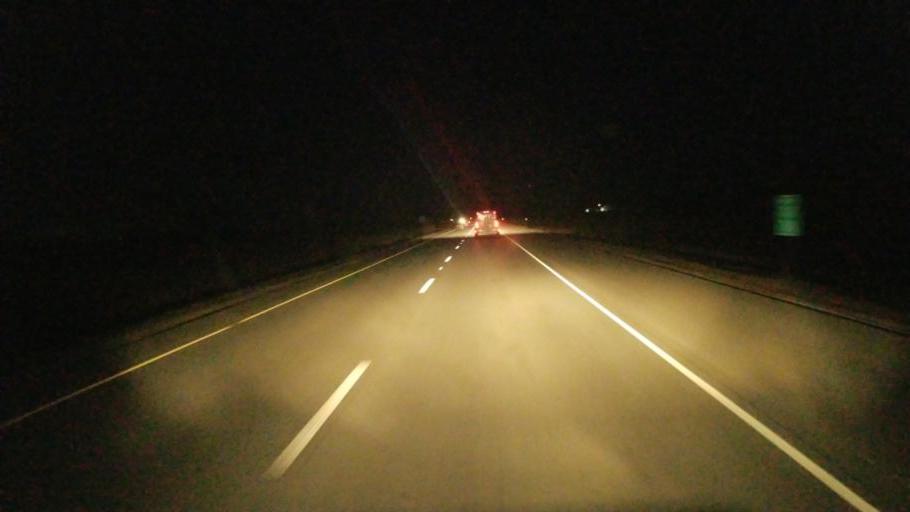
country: US
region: Illinois
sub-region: Henderson County
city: Oquawka
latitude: 40.8471
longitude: -90.9137
